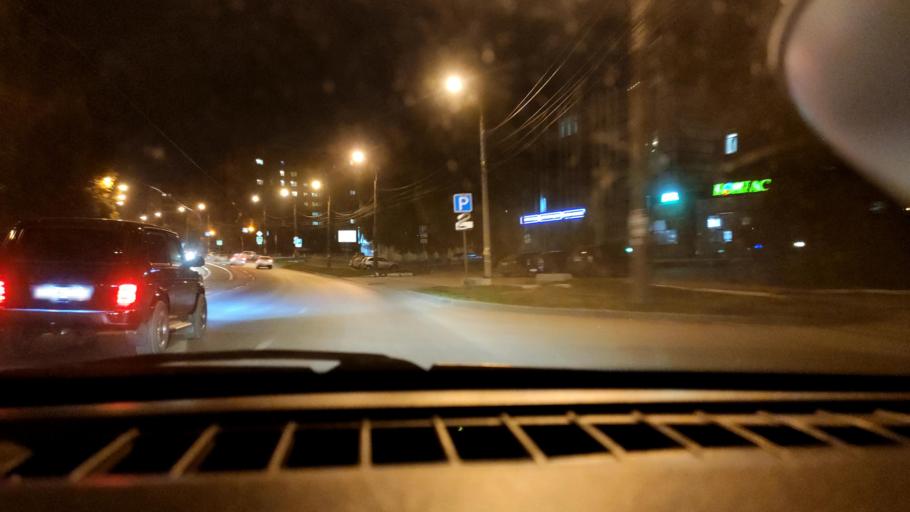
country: RU
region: Samara
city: Samara
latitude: 53.1908
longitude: 50.1694
